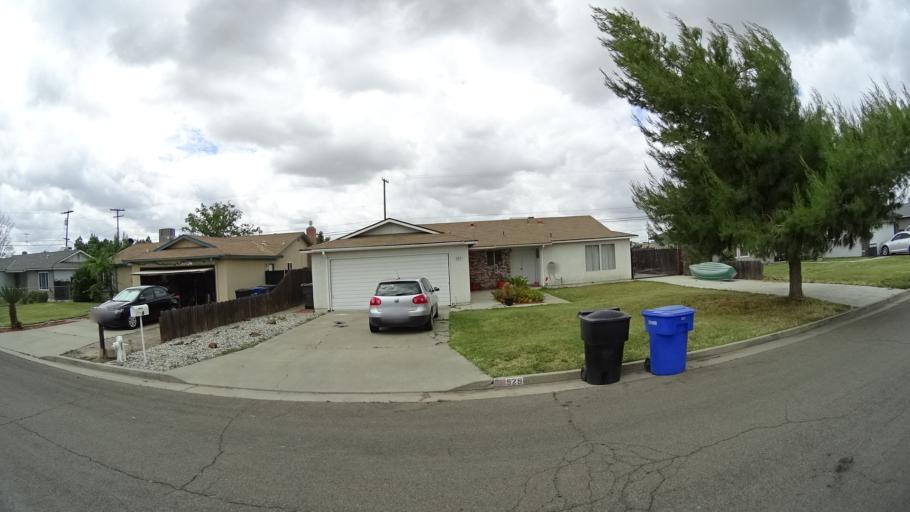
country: US
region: California
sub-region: Kings County
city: Hanford
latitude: 36.3321
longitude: -119.6303
